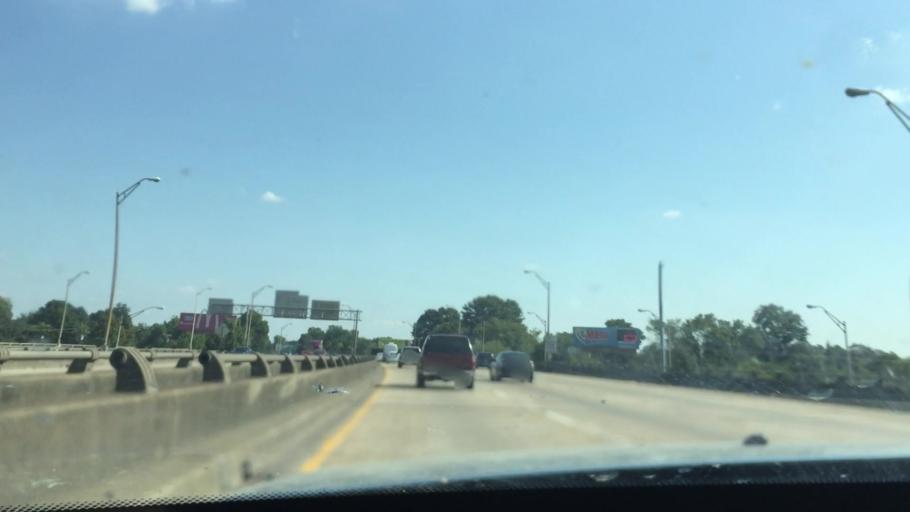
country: US
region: Louisiana
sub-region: East Baton Rouge Parish
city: Baton Rouge
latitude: 30.4325
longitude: -91.1753
